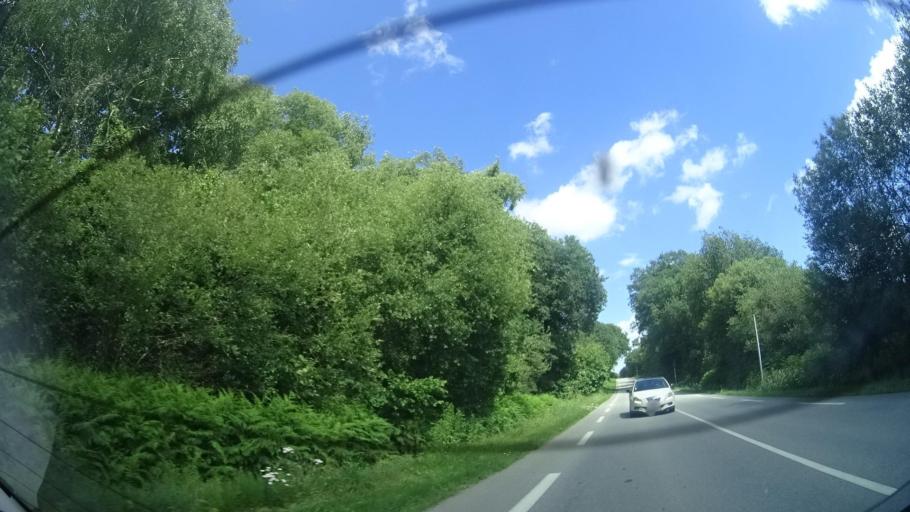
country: FR
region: Brittany
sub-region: Departement du Morbihan
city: Malansac
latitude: 47.6658
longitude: -2.2922
